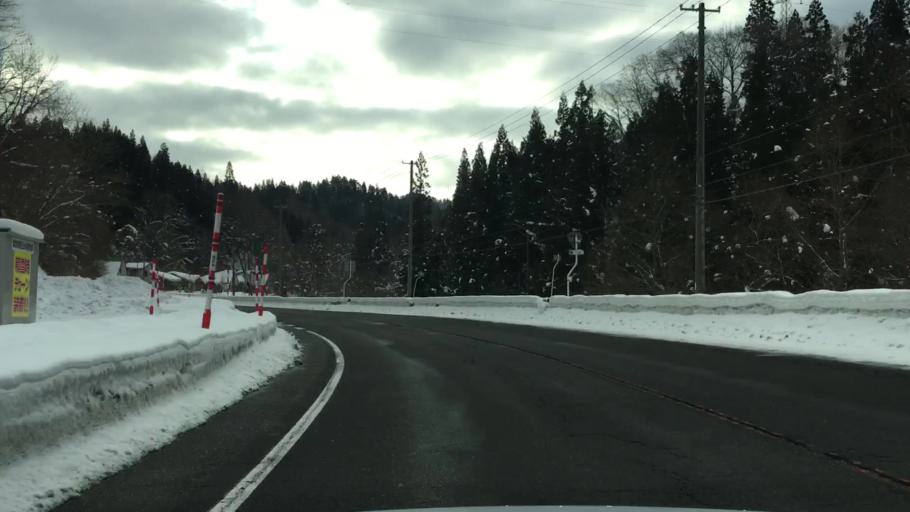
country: JP
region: Akita
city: Odate
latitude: 40.4333
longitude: 140.6348
